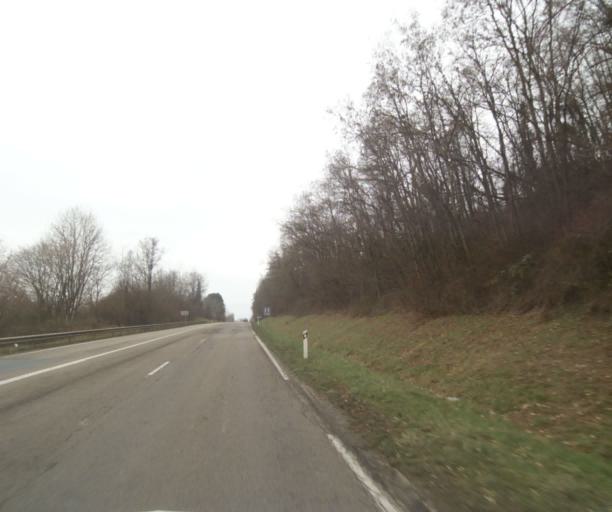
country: FR
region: Champagne-Ardenne
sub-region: Departement de la Haute-Marne
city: Bienville
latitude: 48.5901
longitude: 5.0309
